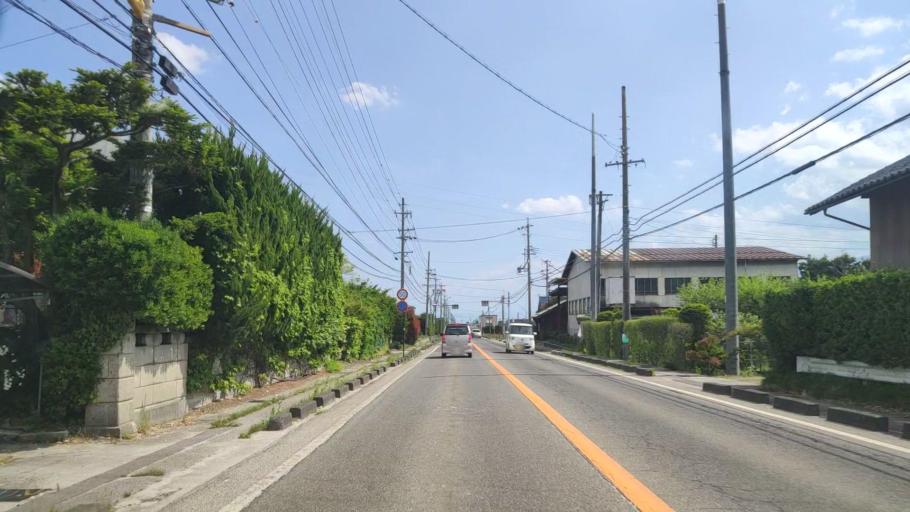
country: JP
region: Nagano
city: Omachi
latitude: 36.4604
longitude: 137.8504
